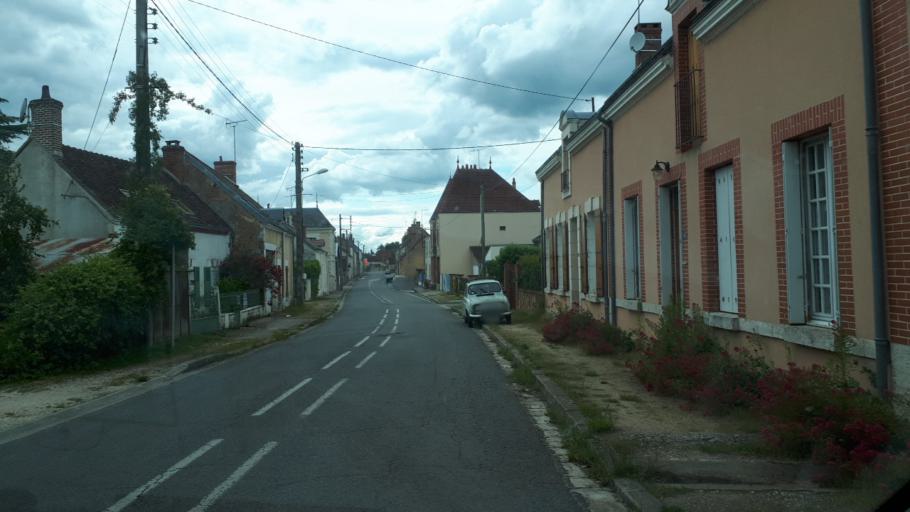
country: FR
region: Centre
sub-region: Departement du Cher
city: Gracay
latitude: 47.1431
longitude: 1.8516
